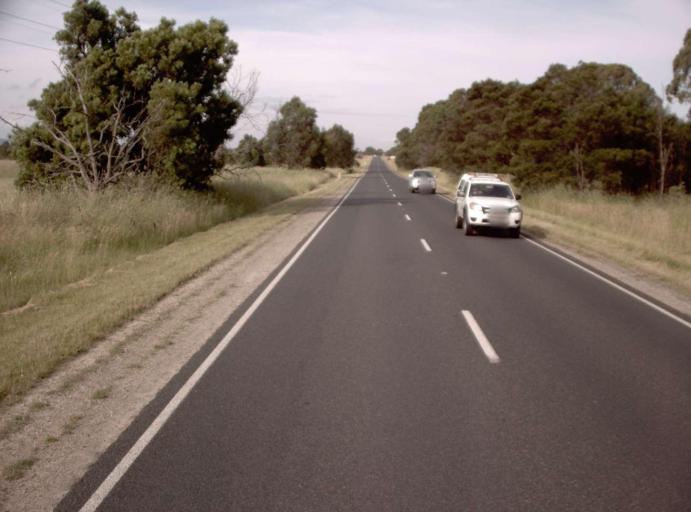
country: AU
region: Victoria
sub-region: Latrobe
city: Traralgon
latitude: -38.1167
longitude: 146.5787
